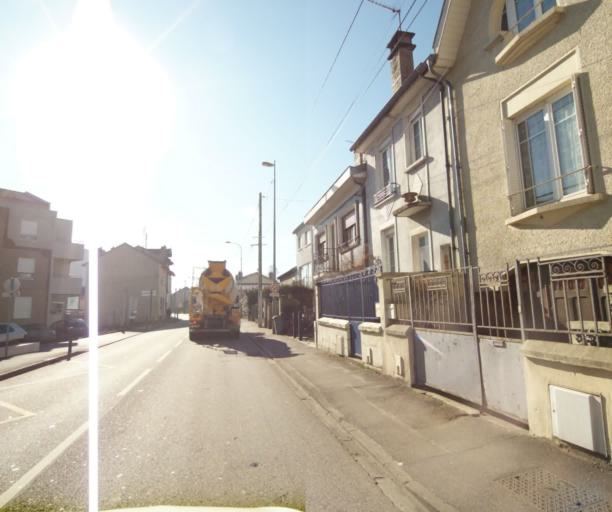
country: FR
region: Lorraine
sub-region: Departement de Meurthe-et-Moselle
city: Maxeville
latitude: 48.7077
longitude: 6.1721
